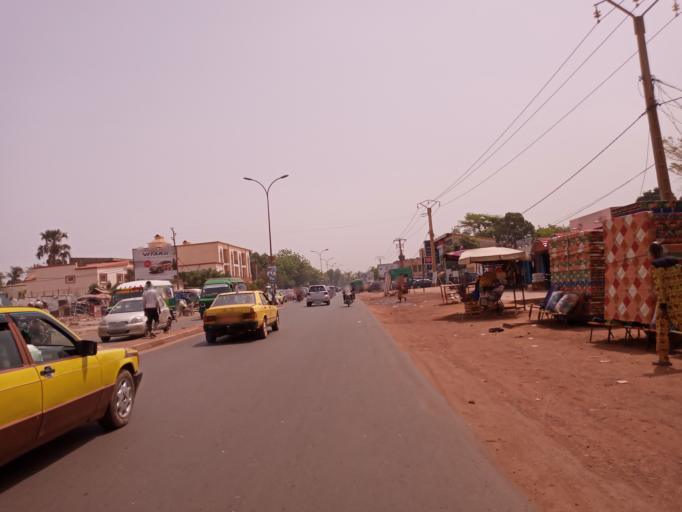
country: ML
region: Bamako
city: Bamako
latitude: 12.6623
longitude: -7.9530
